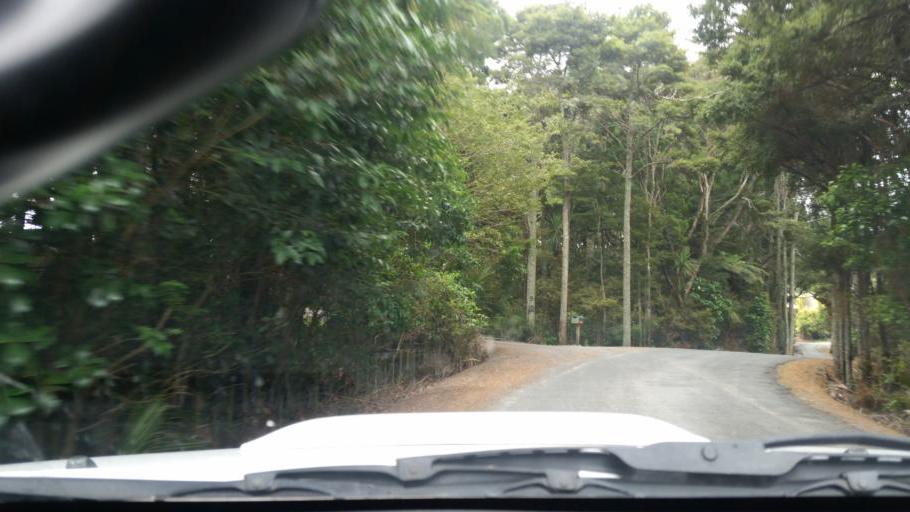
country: NZ
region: Northland
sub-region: Whangarei
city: Ruakaka
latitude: -36.0967
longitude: 174.3523
